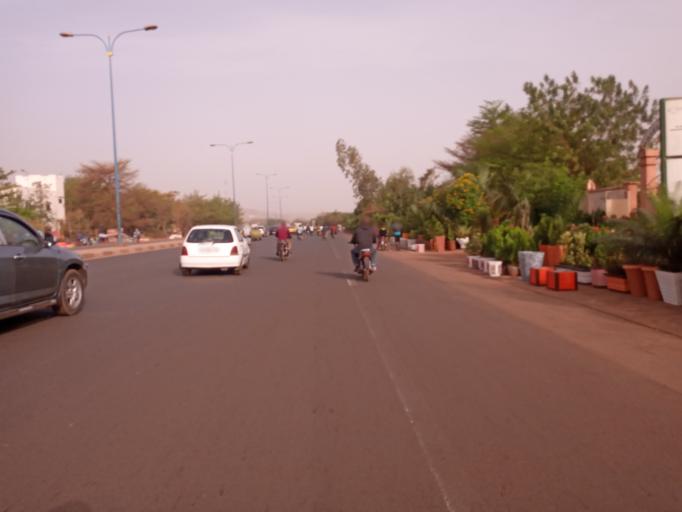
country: ML
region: Bamako
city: Bamako
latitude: 12.6352
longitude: -8.0143
